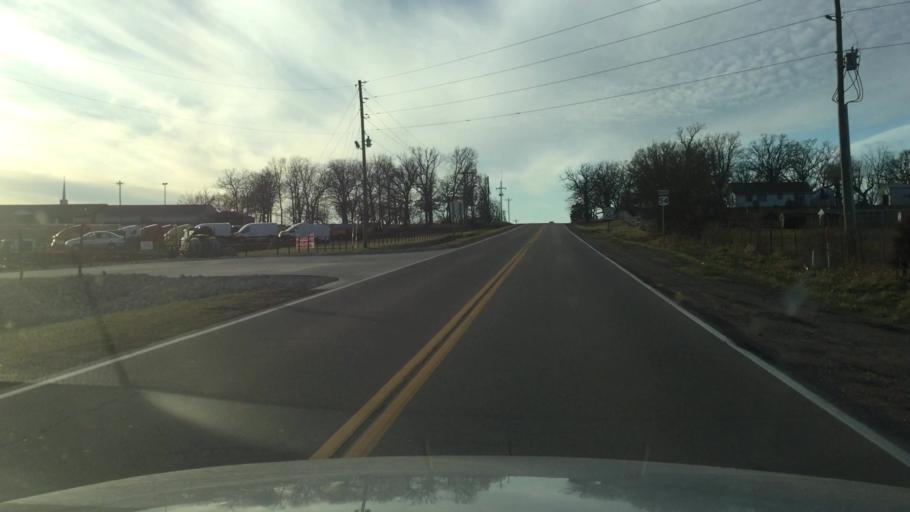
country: US
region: Missouri
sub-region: Miller County
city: Eldon
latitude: 38.3641
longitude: -92.5494
